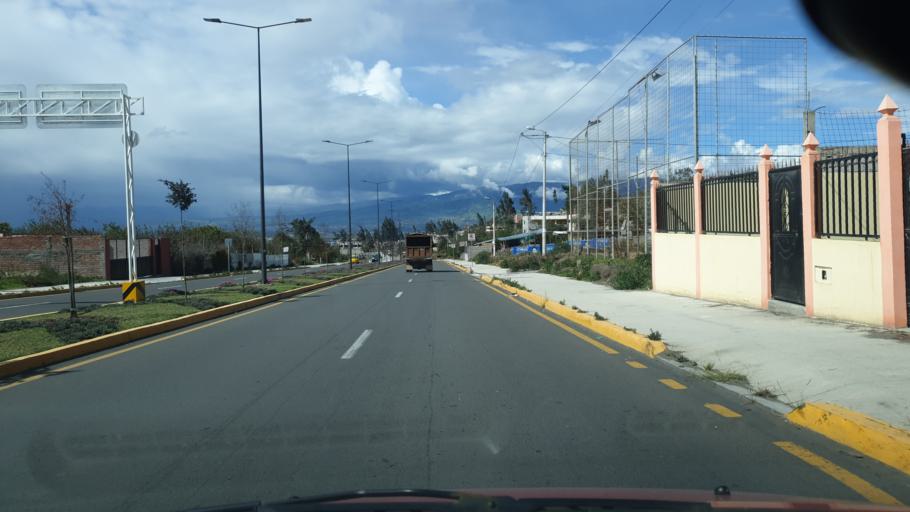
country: EC
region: Tungurahua
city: Ambato
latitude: -1.2960
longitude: -78.6348
